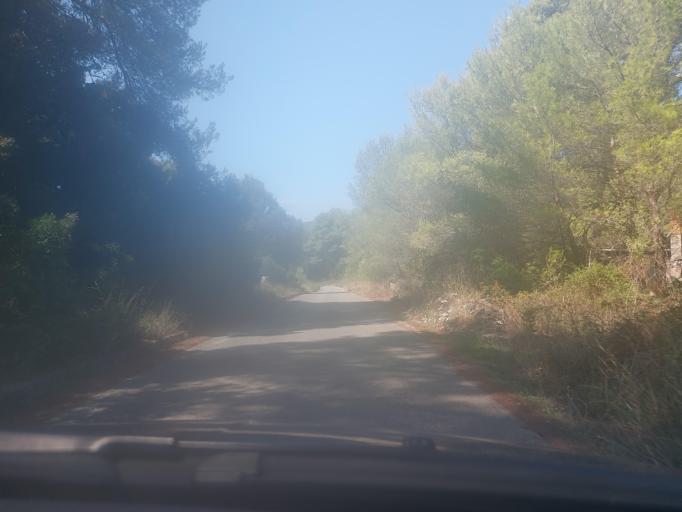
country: HR
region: Dubrovacko-Neretvanska
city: Smokvica
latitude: 42.7464
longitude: 16.8359
